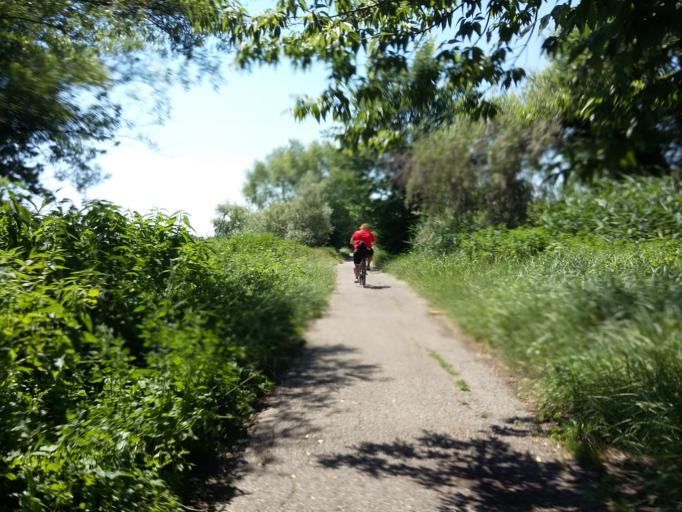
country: AT
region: Lower Austria
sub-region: Politischer Bezirk Ganserndorf
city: Marchegg
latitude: 48.2602
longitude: 16.9562
